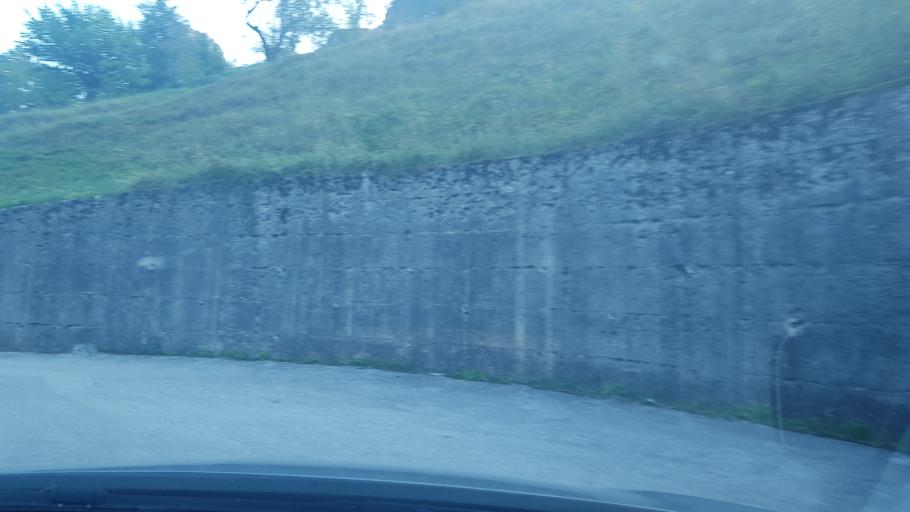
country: IT
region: Friuli Venezia Giulia
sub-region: Provincia di Udine
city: Moggio Udinese
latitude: 46.4274
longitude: 13.2064
